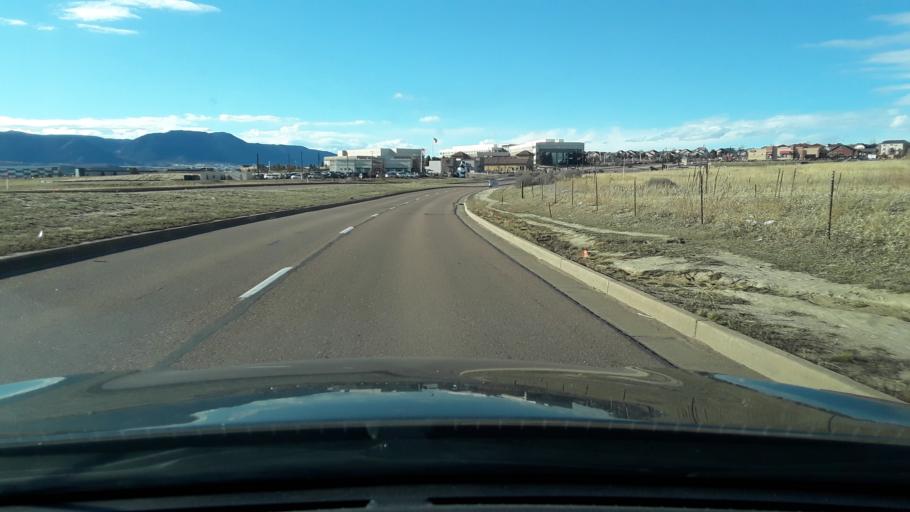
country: US
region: Colorado
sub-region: El Paso County
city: Gleneagle
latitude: 39.0218
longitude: -104.8151
